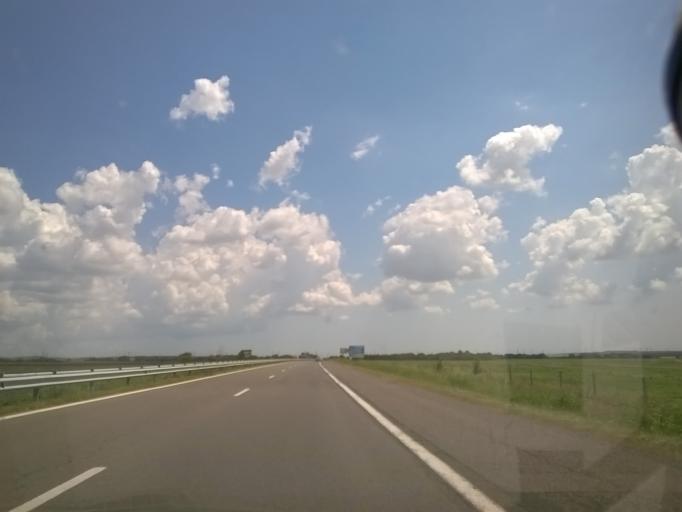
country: BG
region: Burgas
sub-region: Obshtina Kameno
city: Kameno
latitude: 42.6036
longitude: 27.3307
